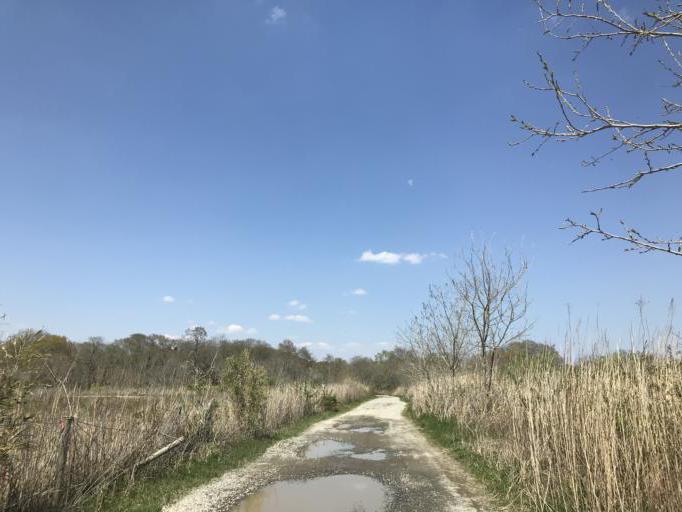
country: JP
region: Ibaraki
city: Moriya
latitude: 35.9190
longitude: 139.9912
